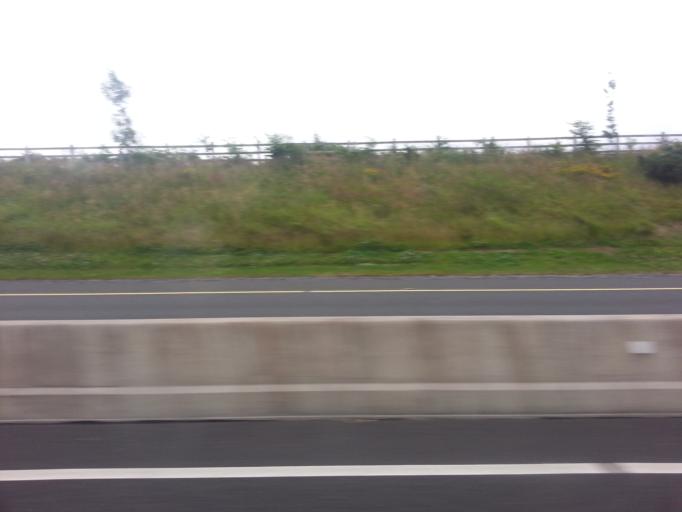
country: IE
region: Leinster
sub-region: County Carlow
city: Bagenalstown
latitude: 52.6657
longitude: -7.0656
